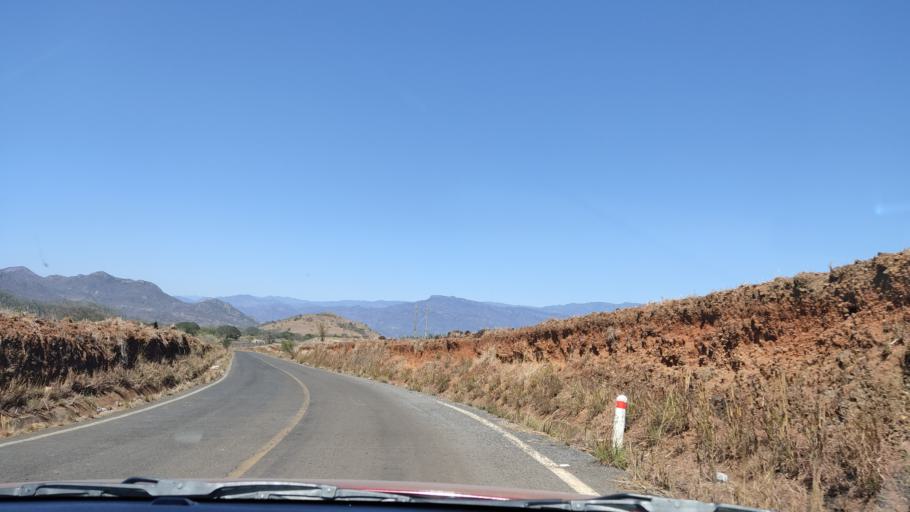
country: MX
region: Nayarit
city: Santa Maria del Oro
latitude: 21.4899
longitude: -104.6236
